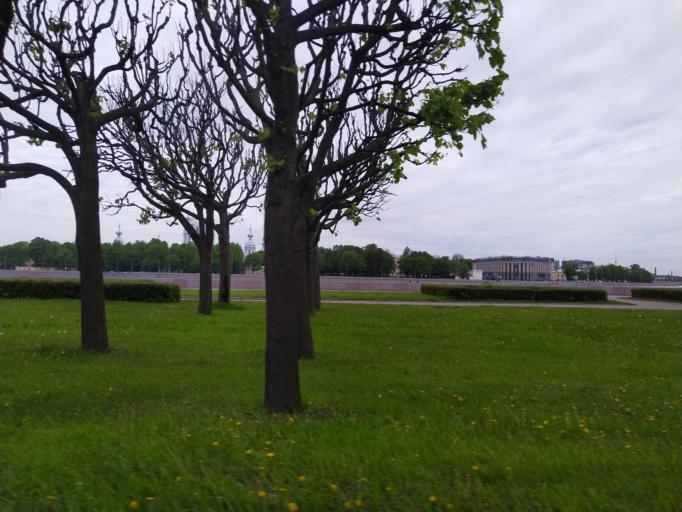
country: RU
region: Leningrad
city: Finlyandskiy
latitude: 59.9500
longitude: 30.4070
